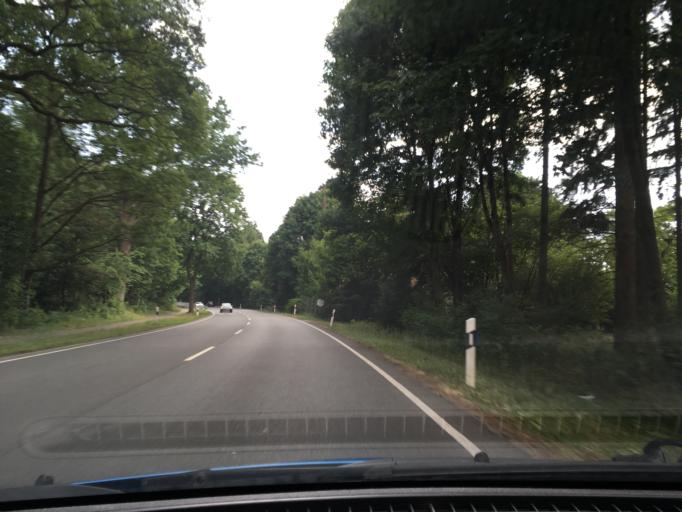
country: DE
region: Lower Saxony
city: Kakenstorf
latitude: 53.2914
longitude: 9.7931
